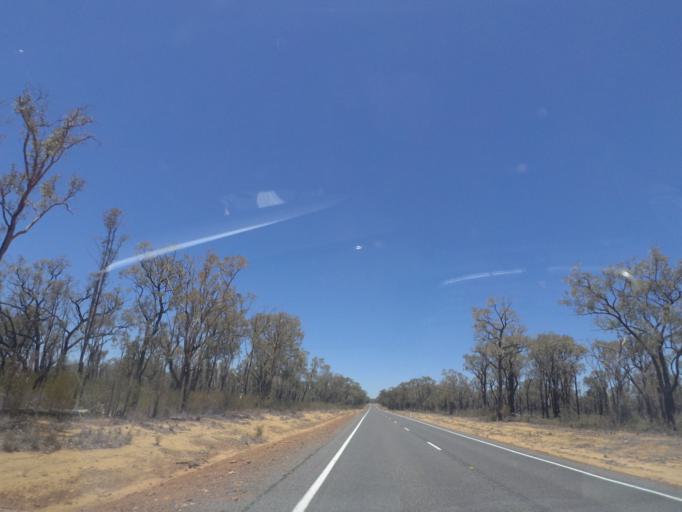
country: AU
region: New South Wales
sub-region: Narrabri
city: Narrabri
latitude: -30.7071
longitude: 149.5318
